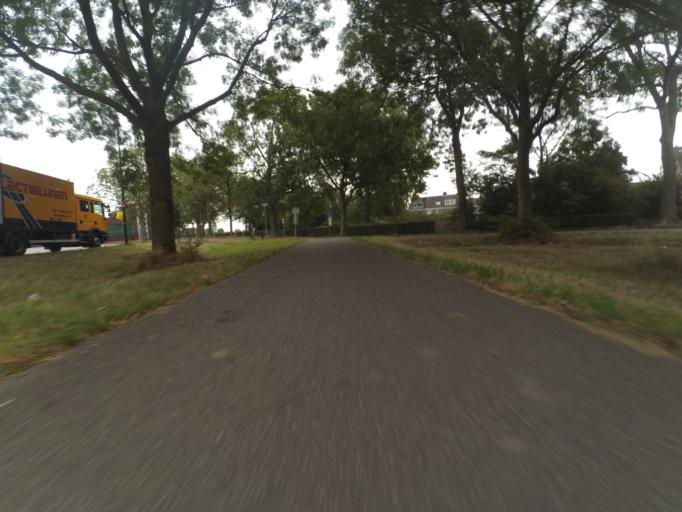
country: NL
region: Utrecht
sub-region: Gemeente Wijk bij Duurstede
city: Wijk bij Duurstede
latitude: 51.9825
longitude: 5.3415
